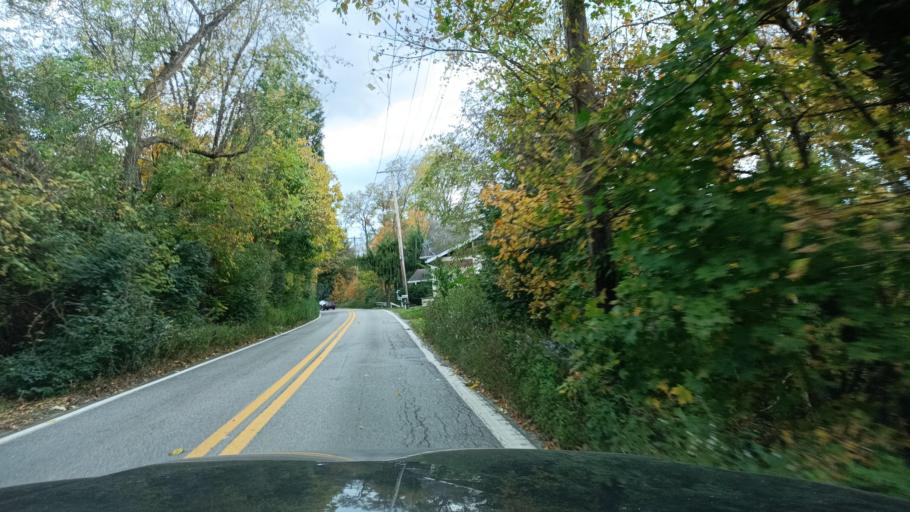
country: US
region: West Virginia
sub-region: Monongalia County
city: Morgantown
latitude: 39.6450
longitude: -79.9464
